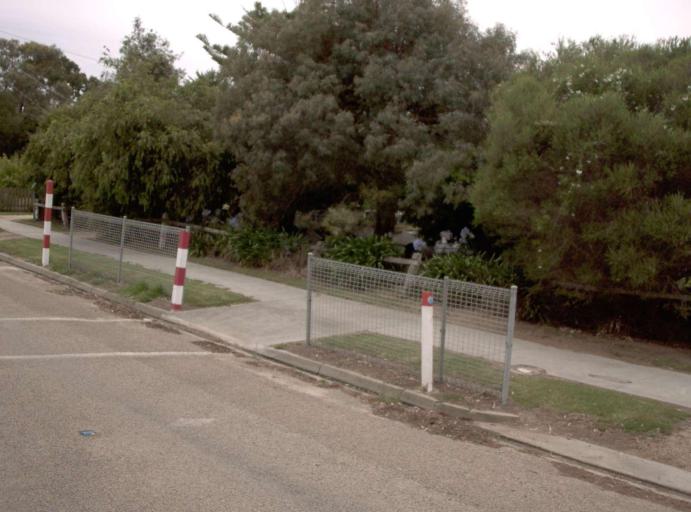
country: AU
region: Victoria
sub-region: East Gippsland
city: Bairnsdale
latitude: -37.8270
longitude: 147.4342
